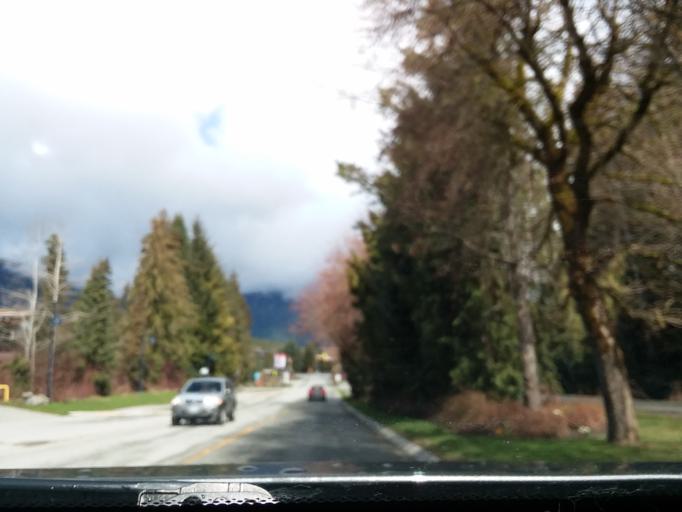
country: CA
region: British Columbia
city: Whistler
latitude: 50.1181
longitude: -122.9538
